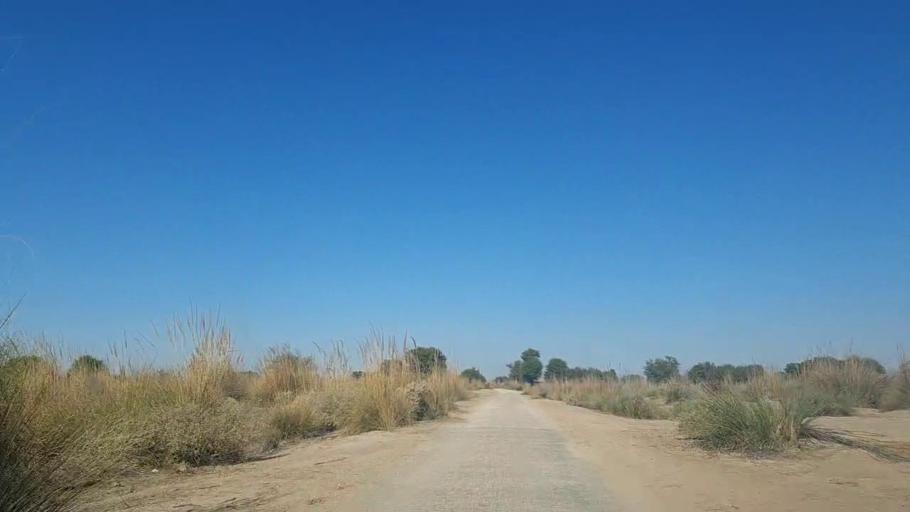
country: PK
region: Sindh
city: Khadro
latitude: 26.2152
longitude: 68.8603
